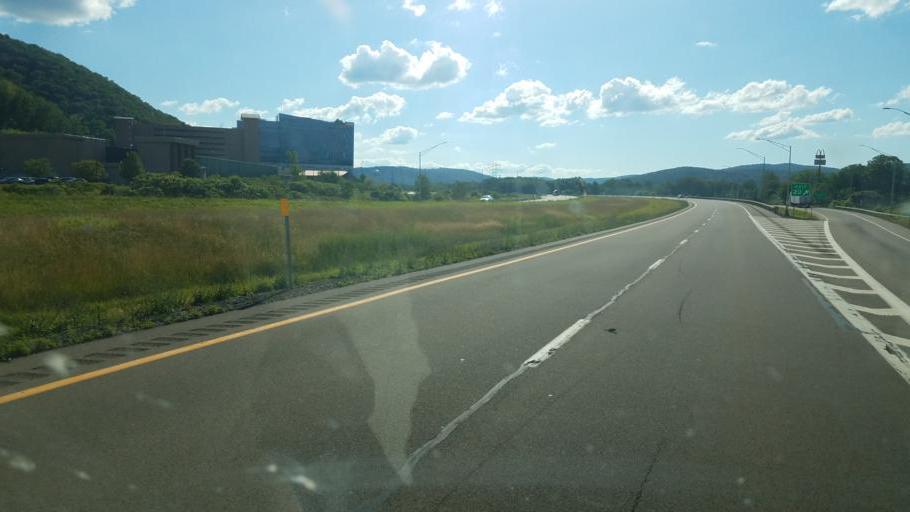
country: US
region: New York
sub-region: Cattaraugus County
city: Salamanca
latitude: 42.1536
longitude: -78.7432
